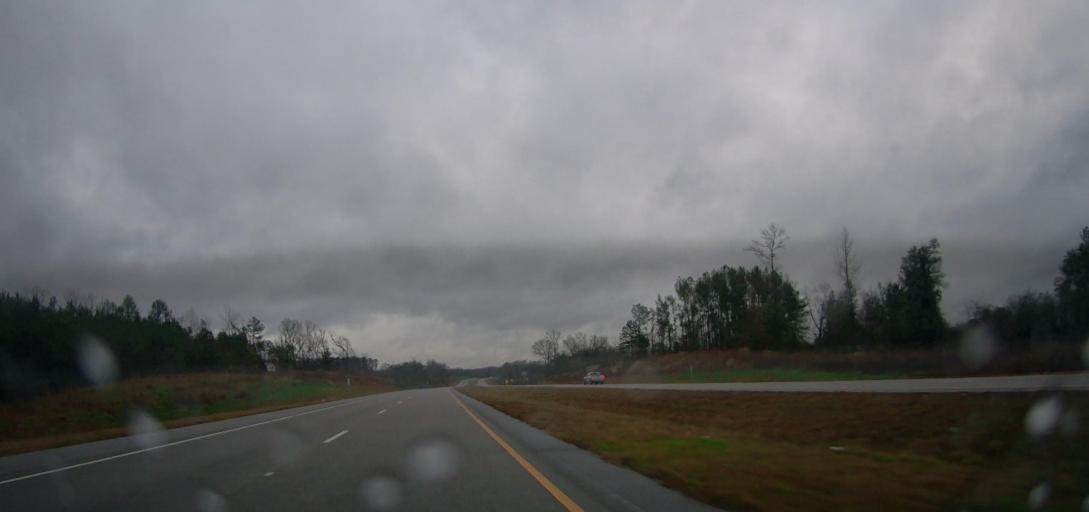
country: US
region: Alabama
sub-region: Bibb County
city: Centreville
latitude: 32.9427
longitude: -87.0795
